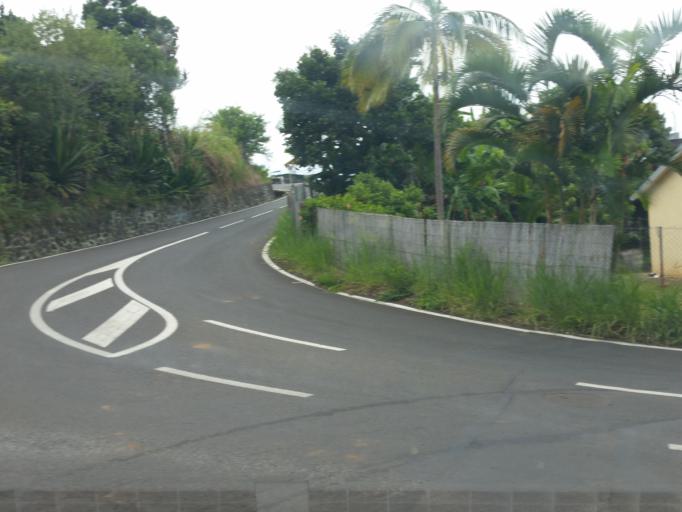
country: RE
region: Reunion
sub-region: Reunion
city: L'Entre-Deux
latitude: -21.2443
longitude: 55.4803
